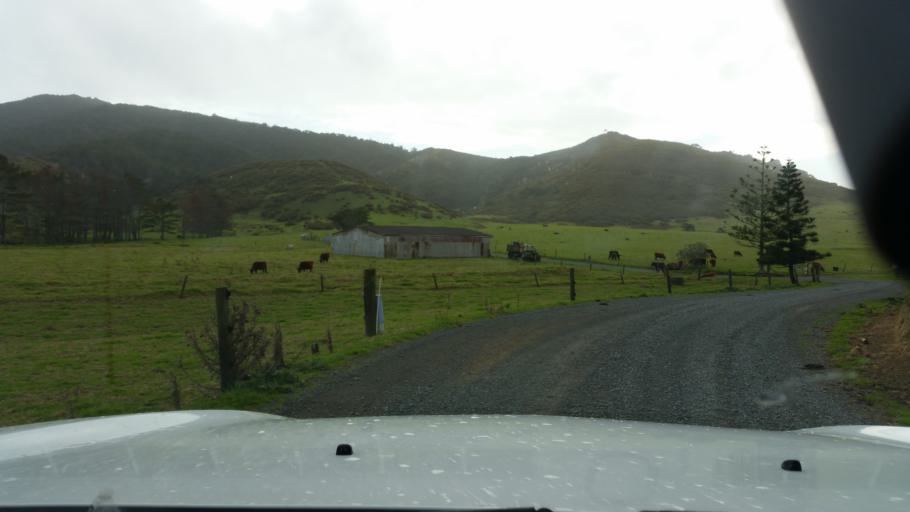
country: NZ
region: Northland
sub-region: Whangarei
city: Ruakaka
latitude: -35.7843
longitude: 174.5478
